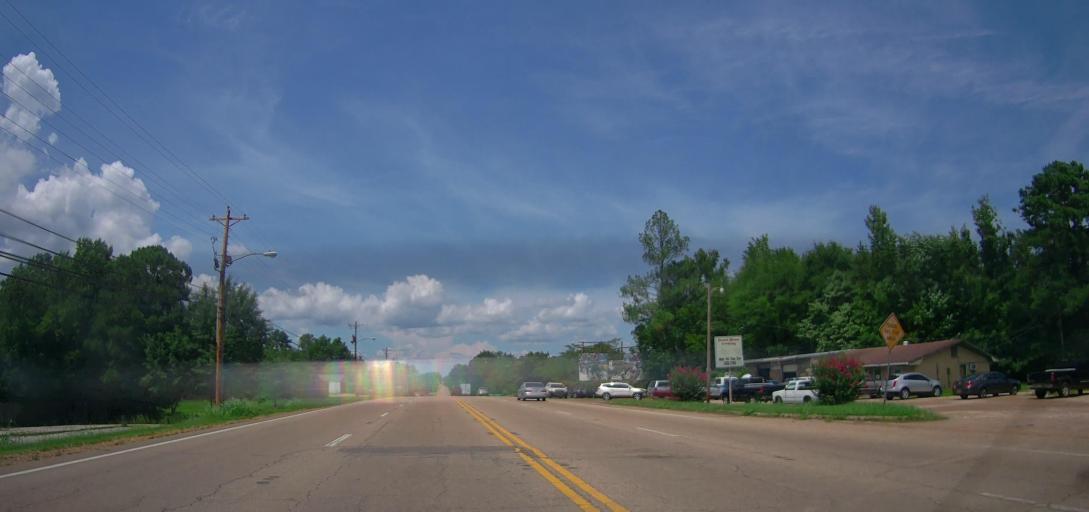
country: US
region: Mississippi
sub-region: Lee County
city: Verona
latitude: 34.1822
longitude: -88.7199
